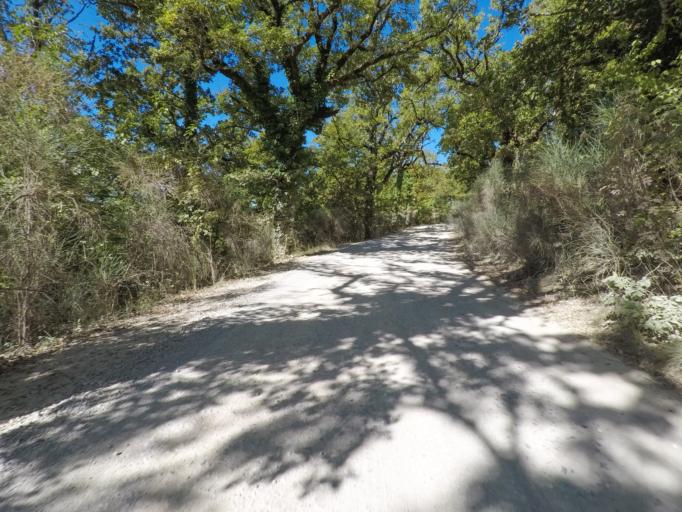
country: IT
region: Tuscany
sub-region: Provincia di Siena
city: Castellina in Chianti
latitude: 43.4294
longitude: 11.3337
